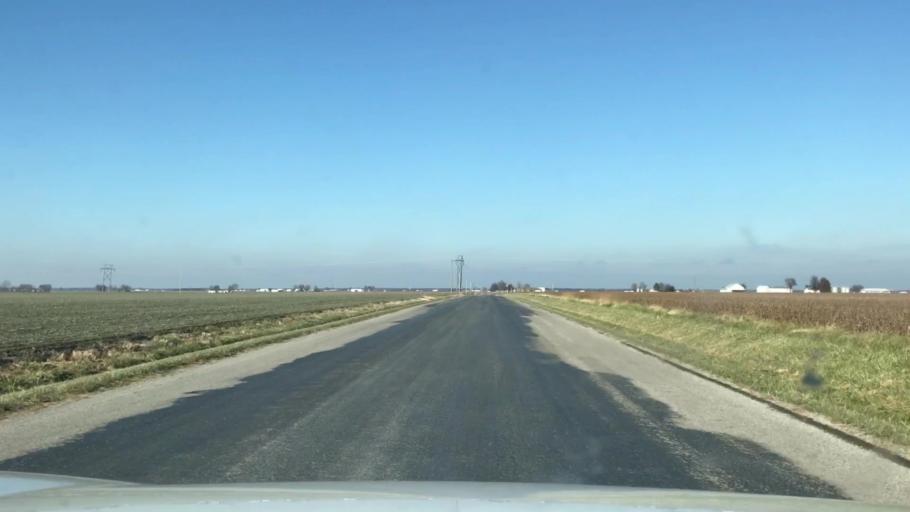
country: US
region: Illinois
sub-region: Washington County
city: Okawville
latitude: 38.3990
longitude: -89.4867
